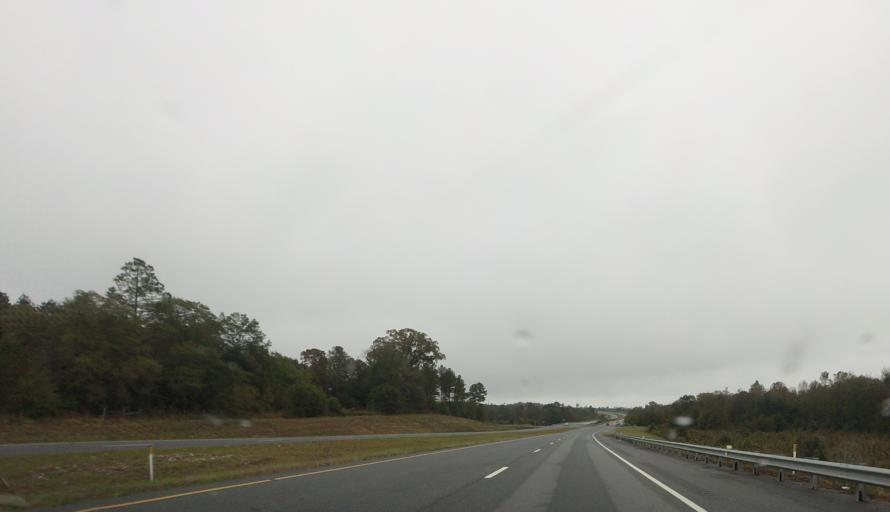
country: US
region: Georgia
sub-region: Taylor County
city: Reynolds
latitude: 32.5459
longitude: -84.0036
